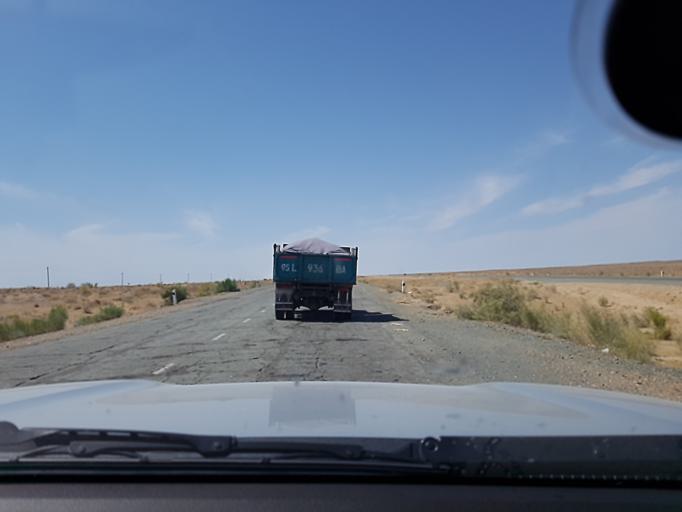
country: UZ
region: Karakalpakstan
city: Mang'it Shahri
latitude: 42.2859
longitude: 60.0805
